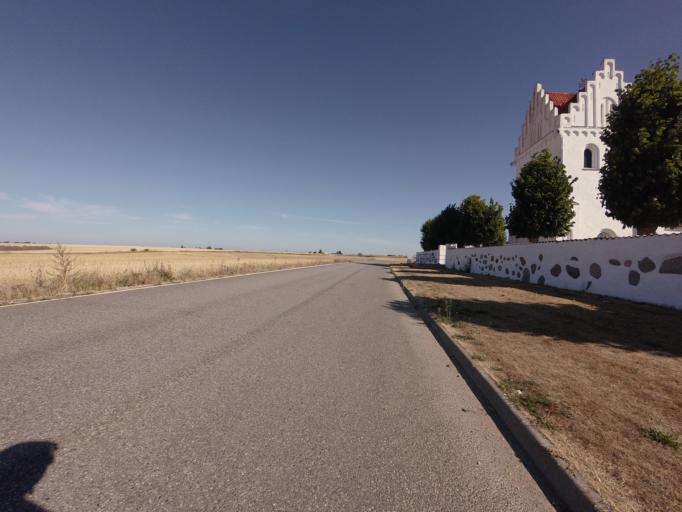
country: SE
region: Skane
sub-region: Trelleborgs Kommun
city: Skare
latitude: 55.4049
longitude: 13.0648
